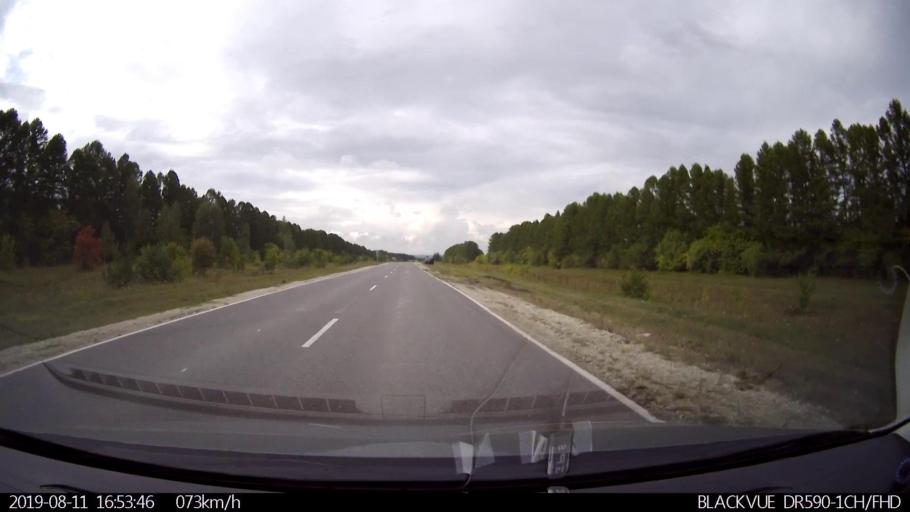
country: RU
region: Ulyanovsk
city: Mayna
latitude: 54.2660
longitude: 47.6690
